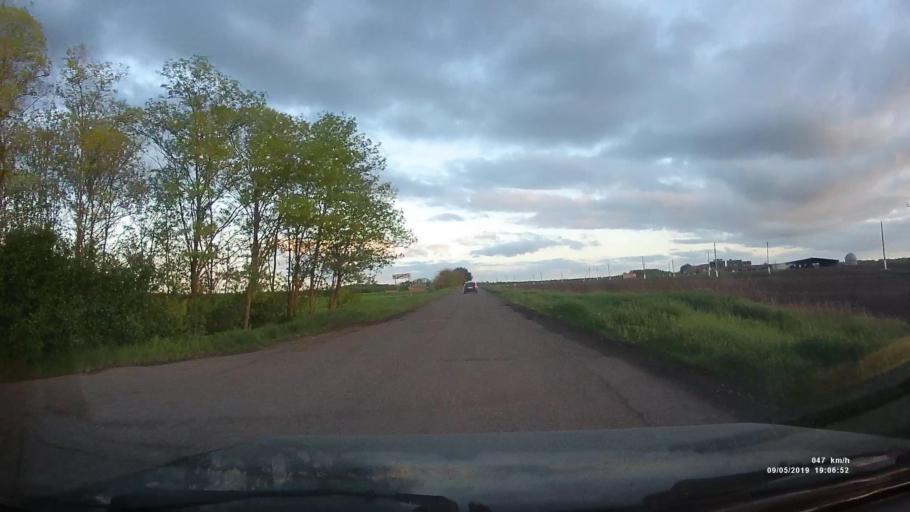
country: RU
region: Krasnodarskiy
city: Kanelovskaya
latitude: 46.7375
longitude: 39.1960
